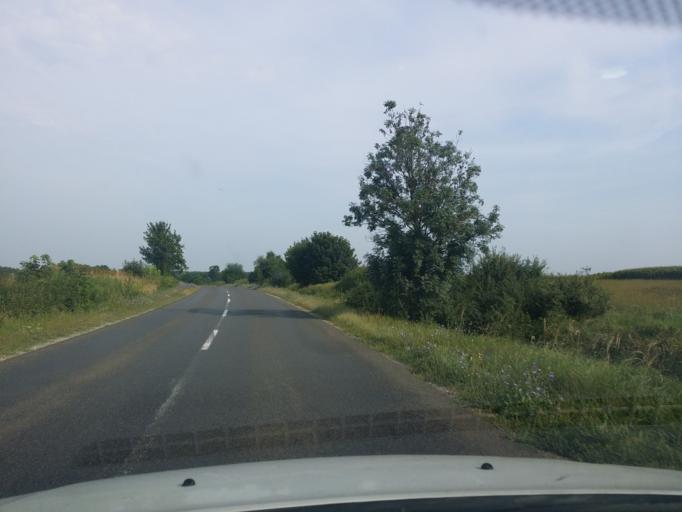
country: HU
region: Pest
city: Galgamacsa
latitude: 47.7214
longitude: 19.3805
